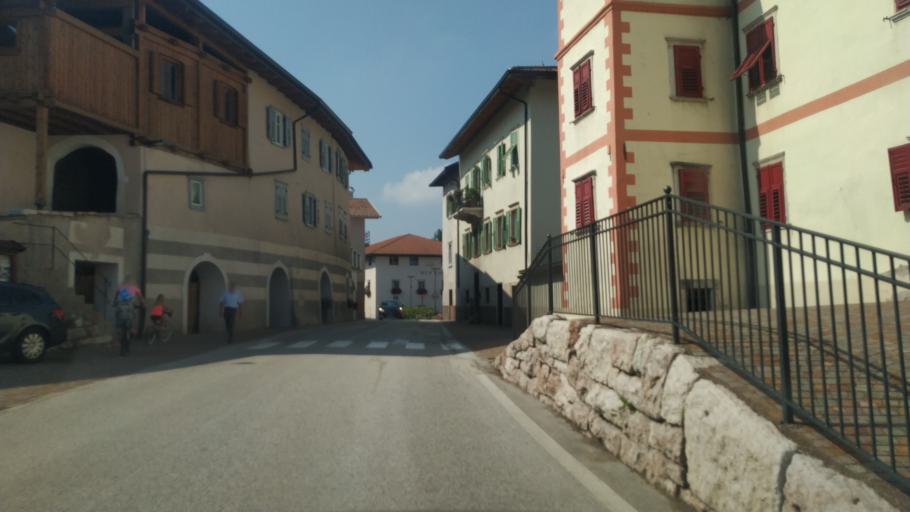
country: IT
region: Trentino-Alto Adige
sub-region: Provincia di Trento
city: Cavareno
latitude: 46.4085
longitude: 11.1372
